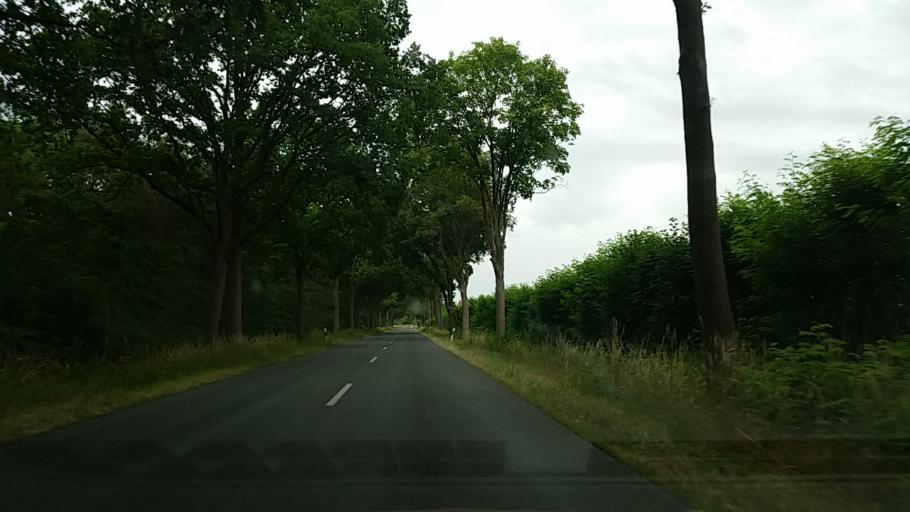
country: DE
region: Lower Saxony
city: Hillerse
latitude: 52.4023
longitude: 10.3517
